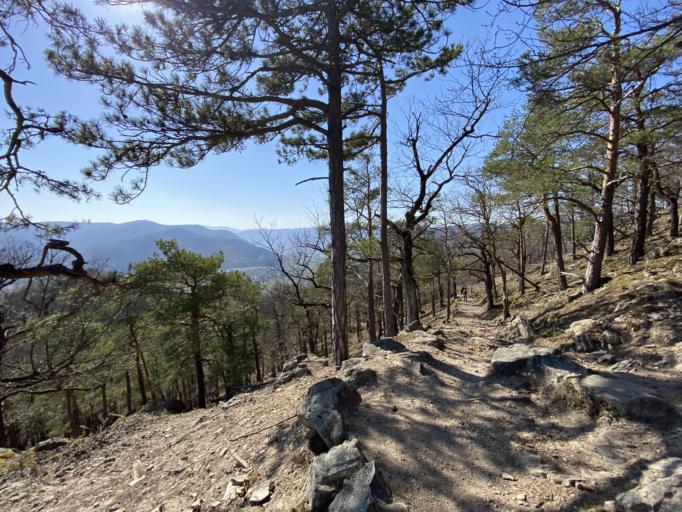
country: AT
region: Lower Austria
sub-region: Politischer Bezirk Krems
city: Durnstein
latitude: 48.4019
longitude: 15.5280
